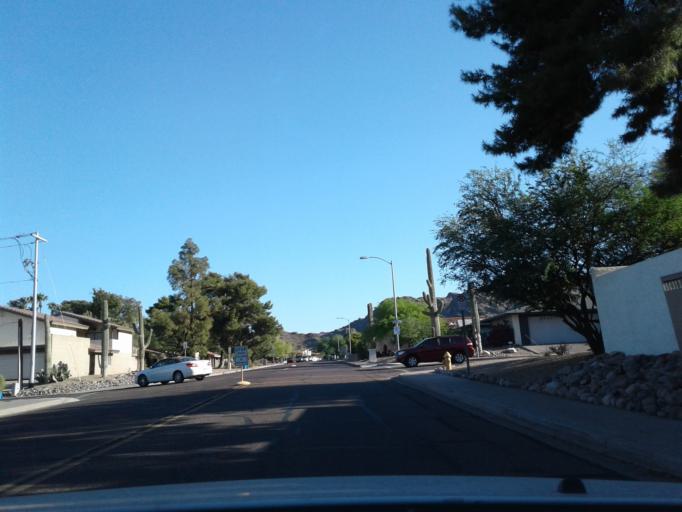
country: US
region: Arizona
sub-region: Maricopa County
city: Paradise Valley
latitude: 33.5416
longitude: -112.0346
